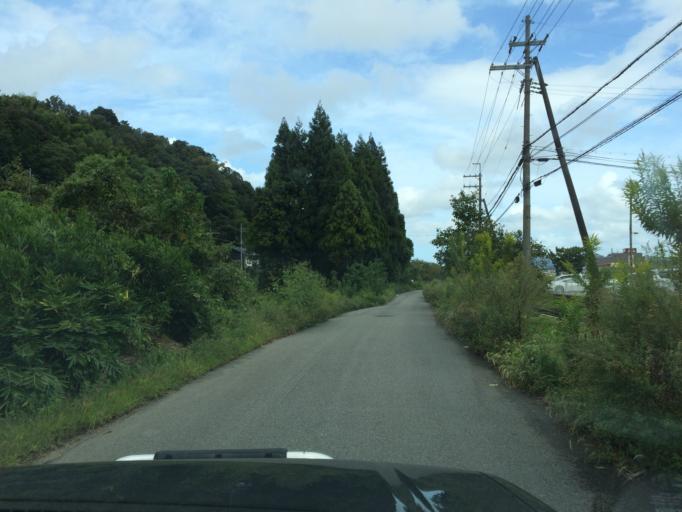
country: JP
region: Hyogo
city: Toyooka
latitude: 35.5036
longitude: 134.8086
